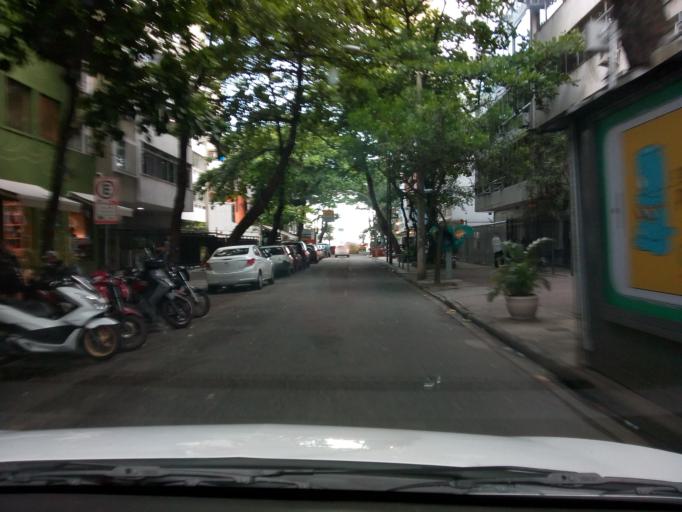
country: BR
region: Rio de Janeiro
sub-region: Rio De Janeiro
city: Rio de Janeiro
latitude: -22.9841
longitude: -43.2071
